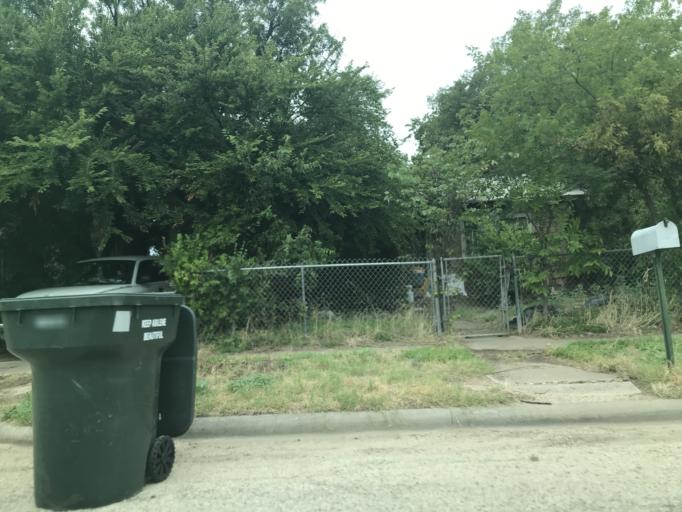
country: US
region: Texas
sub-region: Taylor County
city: Abilene
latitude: 32.4370
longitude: -99.7374
